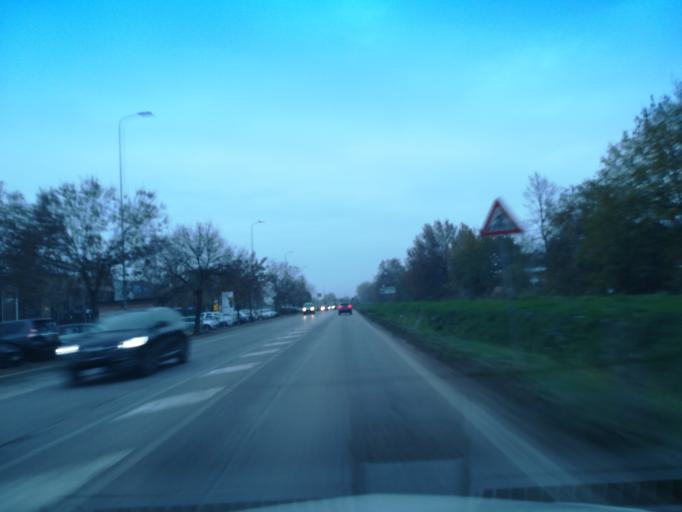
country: IT
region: Emilia-Romagna
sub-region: Provincia di Ravenna
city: Faenza
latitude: 44.3167
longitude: 11.9018
